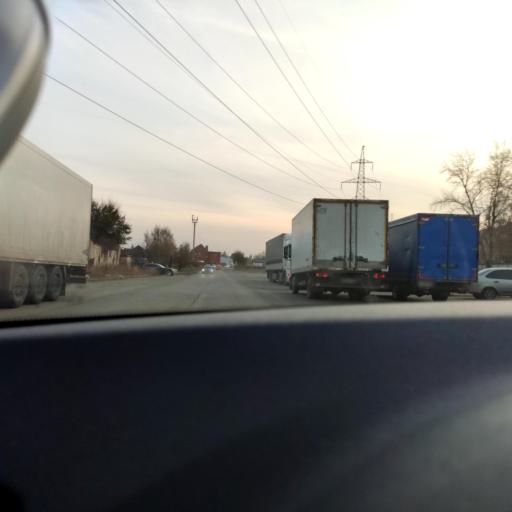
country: RU
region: Samara
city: Petra-Dubrava
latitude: 53.2571
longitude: 50.3124
